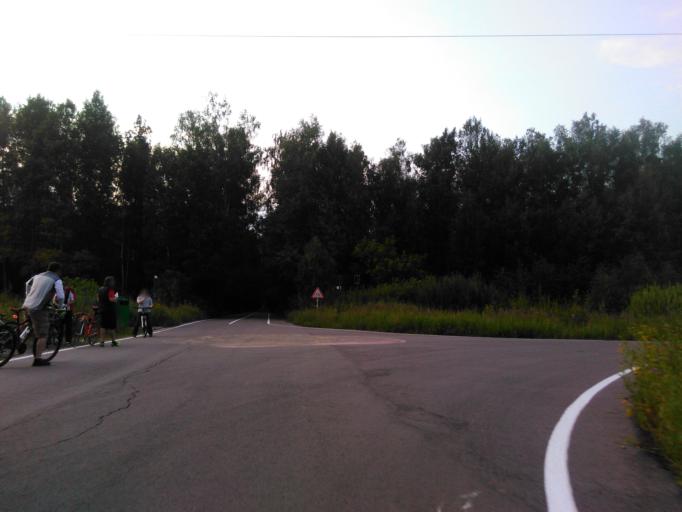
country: RU
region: Moscow
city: Babushkin
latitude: 55.8422
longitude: 37.7268
